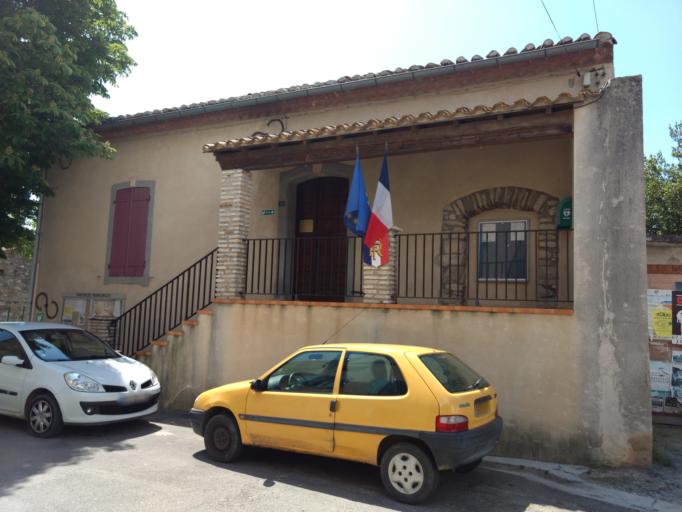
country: FR
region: Languedoc-Roussillon
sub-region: Departement de l'Herault
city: Olonzac
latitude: 43.3536
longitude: 2.7766
